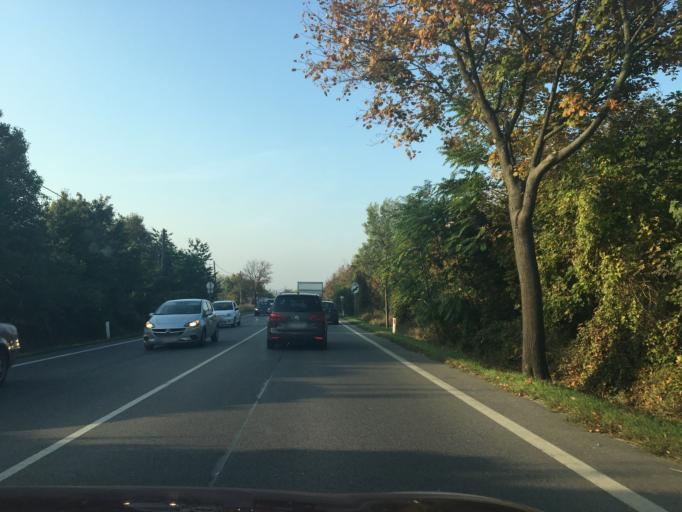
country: AT
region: Lower Austria
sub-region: Politischer Bezirk Korneuburg
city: Hagenbrunn
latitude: 48.3069
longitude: 16.4260
